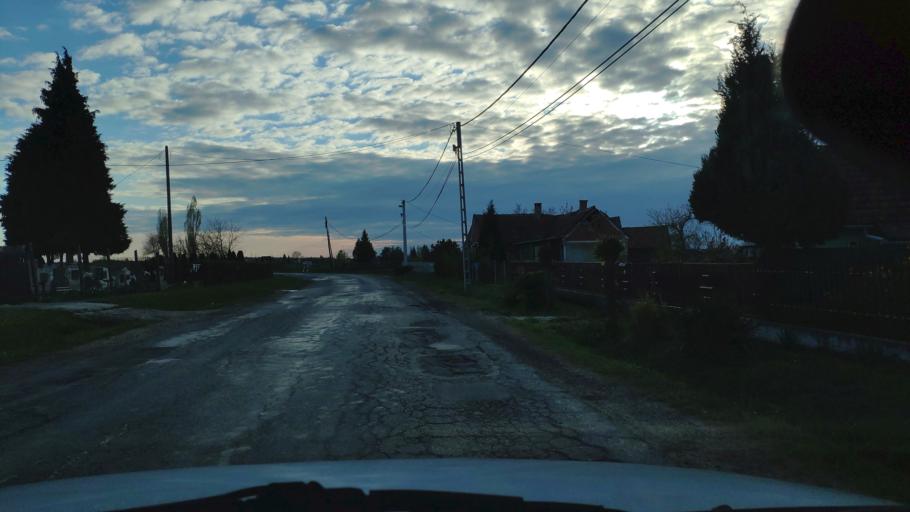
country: HU
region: Zala
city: Nagykanizsa
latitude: 46.4316
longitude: 17.0566
